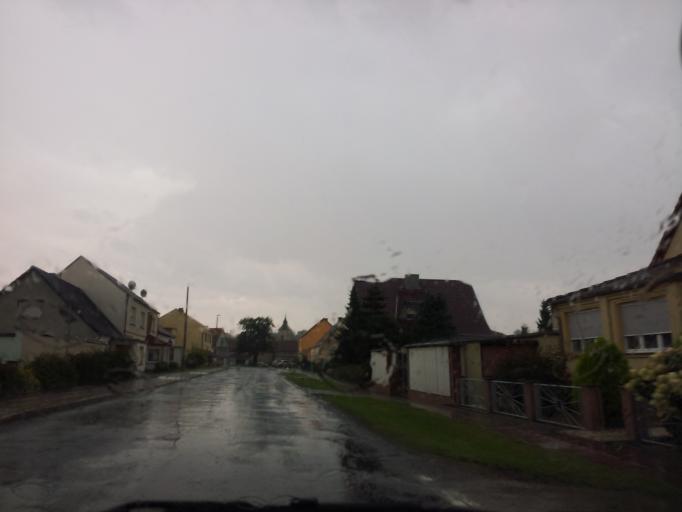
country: DE
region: Brandenburg
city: Wollin
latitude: 52.2836
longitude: 12.4676
